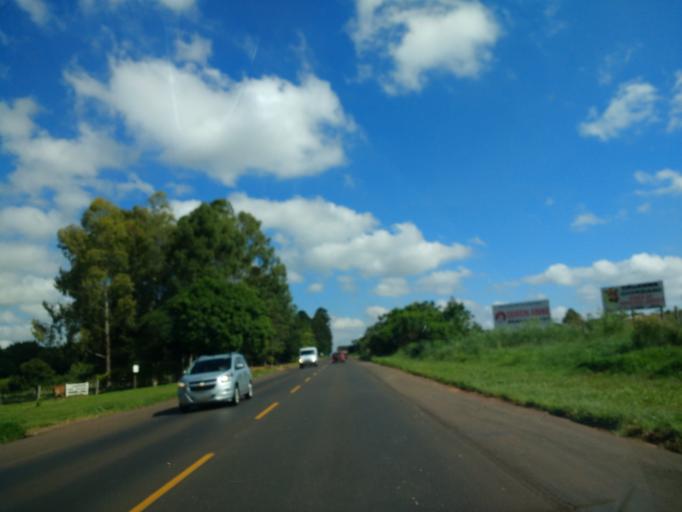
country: BR
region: Parana
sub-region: Umuarama
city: Umuarama
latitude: -23.8368
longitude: -53.3588
